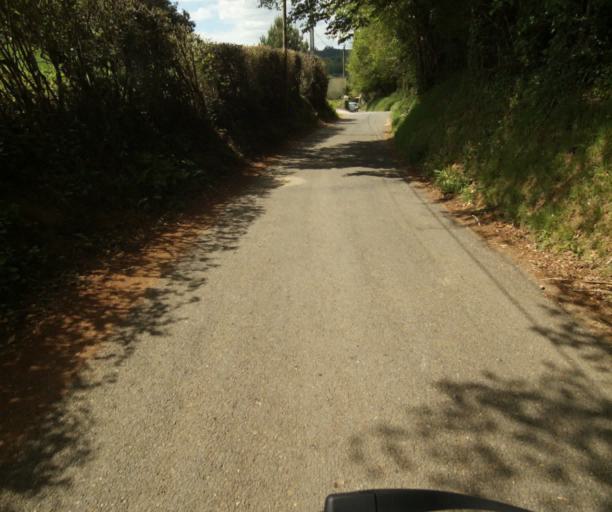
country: FR
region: Limousin
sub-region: Departement de la Correze
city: Tulle
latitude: 45.2845
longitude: 1.7767
